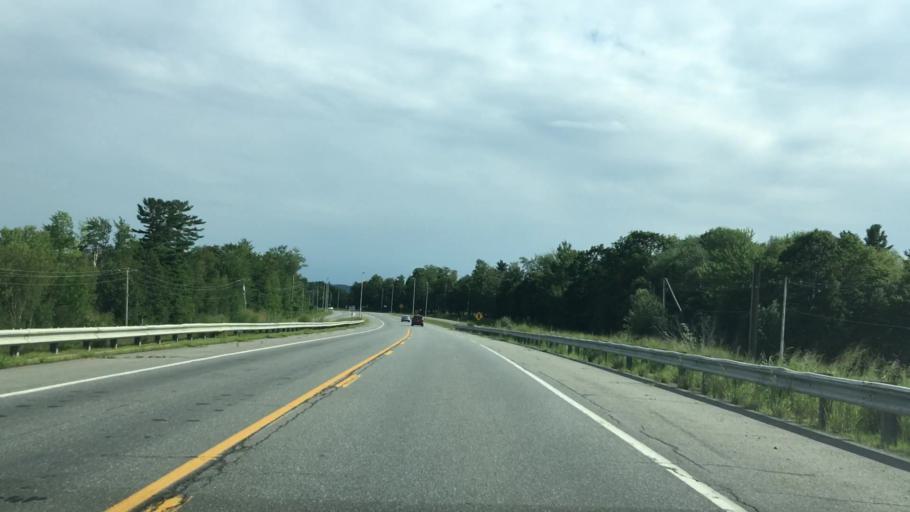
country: US
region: Maine
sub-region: Waldo County
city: Belfast
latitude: 44.4228
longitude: -69.0214
